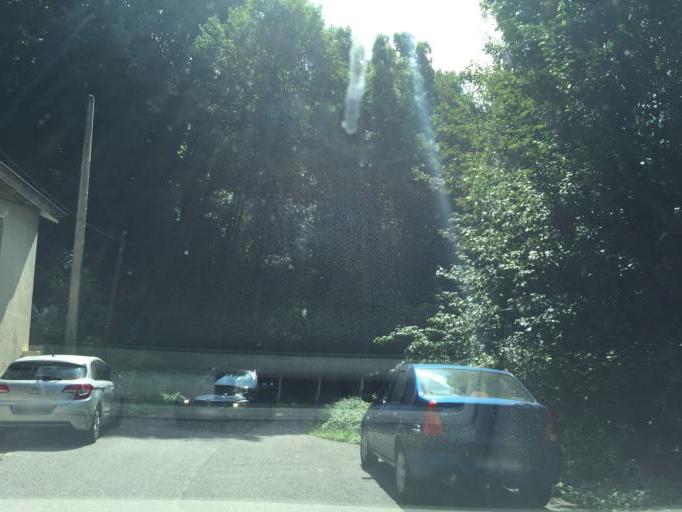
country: FR
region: Rhone-Alpes
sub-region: Departement de la Loire
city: Saint-Jean-Bonnefonds
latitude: 45.4036
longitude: 4.4471
